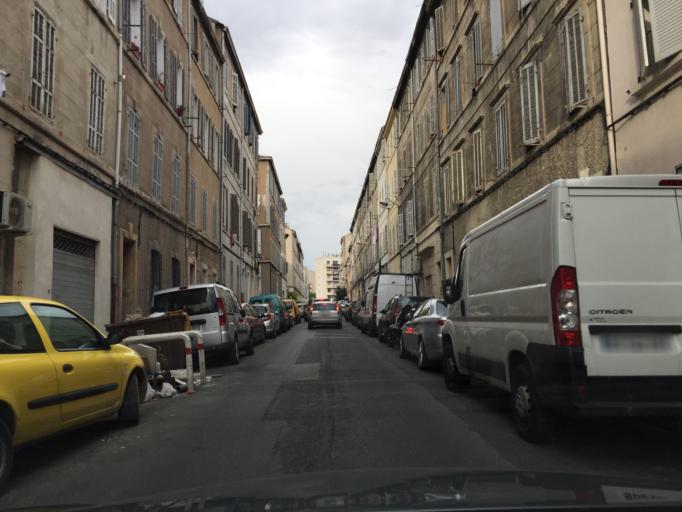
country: FR
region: Provence-Alpes-Cote d'Azur
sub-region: Departement des Bouches-du-Rhone
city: Marseille 01
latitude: 43.3104
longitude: 5.3859
